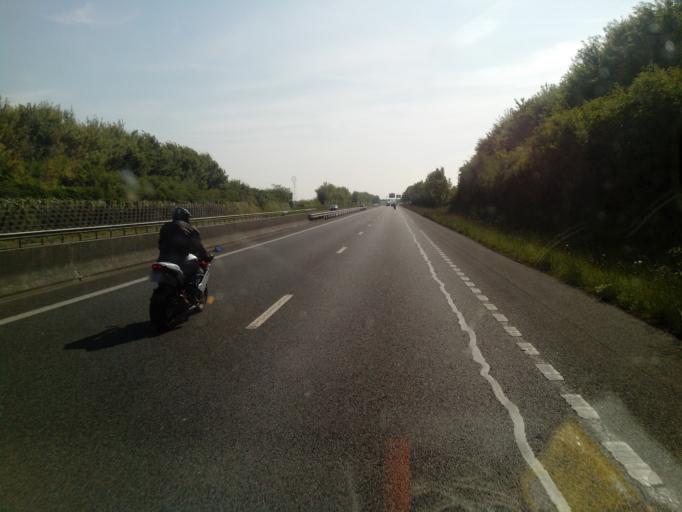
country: FR
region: Picardie
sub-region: Departement de la Somme
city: Oisemont
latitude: 50.0209
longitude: 1.7236
